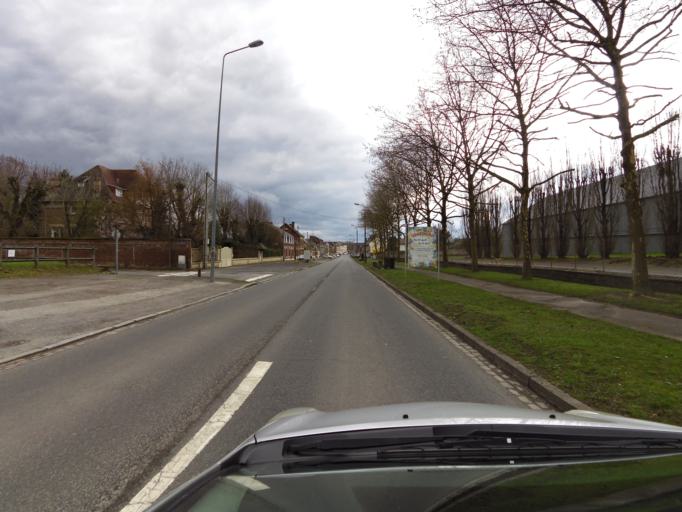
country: FR
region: Picardie
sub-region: Departement de la Somme
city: Roye
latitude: 49.7023
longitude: 2.7951
